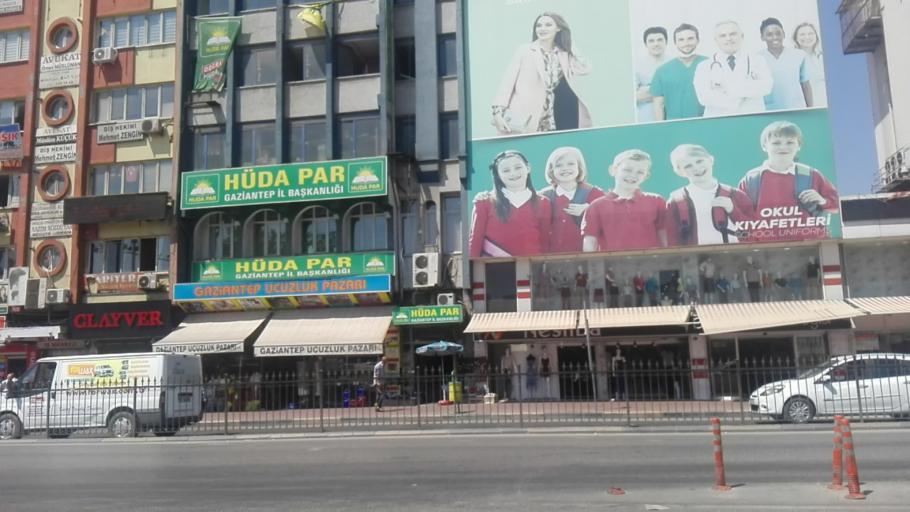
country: TR
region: Gaziantep
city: Gaziantep
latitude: 37.0612
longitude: 37.3799
